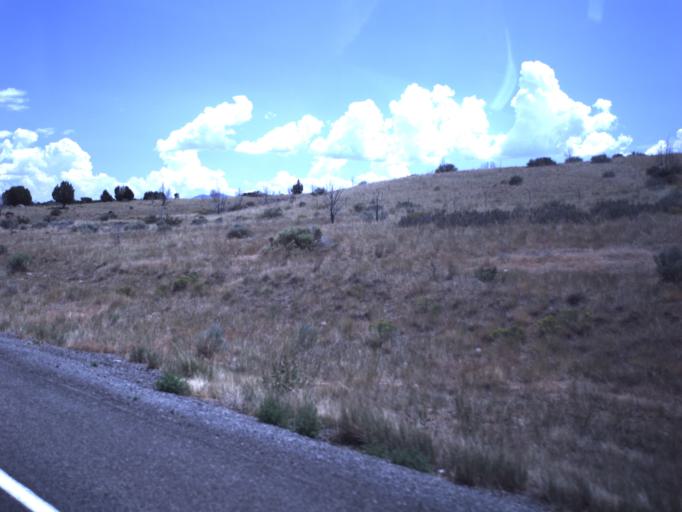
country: US
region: Utah
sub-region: Juab County
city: Nephi
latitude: 39.6592
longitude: -112.0667
